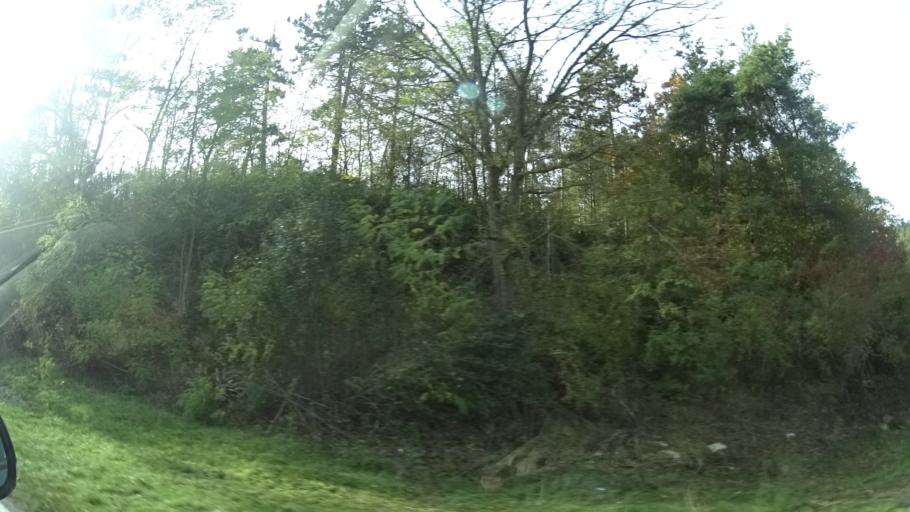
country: DE
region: Baden-Wuerttemberg
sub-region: Regierungsbezirk Stuttgart
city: Bad Mergentheim
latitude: 49.4594
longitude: 9.7666
